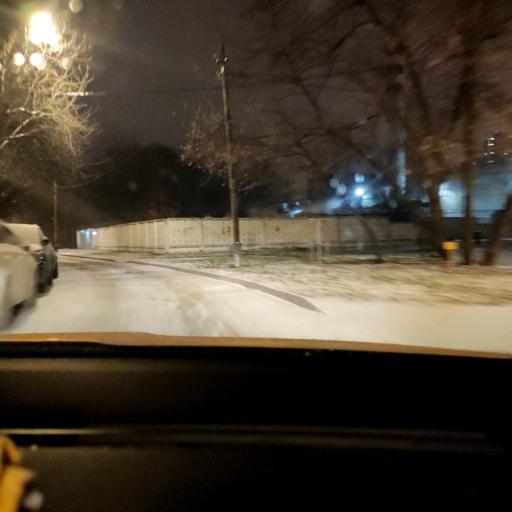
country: RU
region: Moscow
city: Strogino
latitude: 55.8521
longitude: 37.3876
